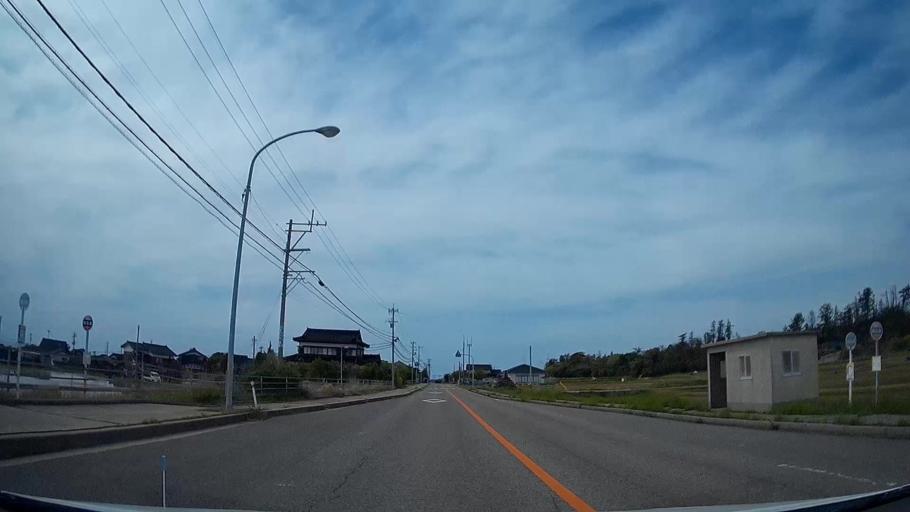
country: JP
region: Ishikawa
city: Hakui
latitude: 37.0355
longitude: 136.7459
